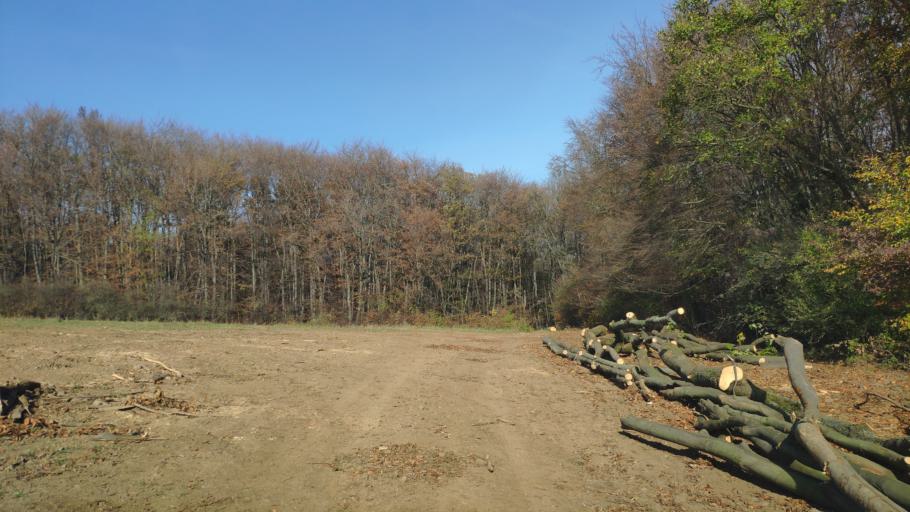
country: SK
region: Presovsky
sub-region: Okres Presov
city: Presov
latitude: 48.8952
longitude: 21.2267
